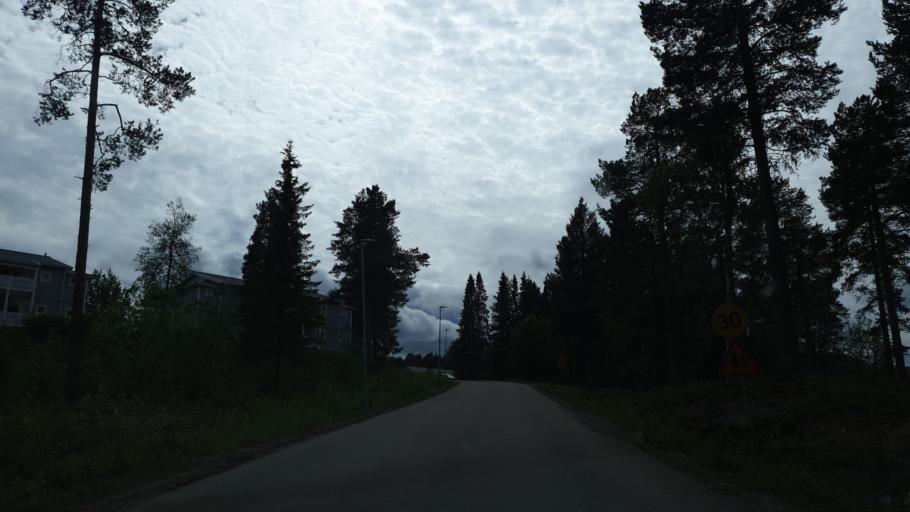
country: SE
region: Norrbotten
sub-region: Gallivare Kommun
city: Gaellivare
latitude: 67.1268
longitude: 20.6580
